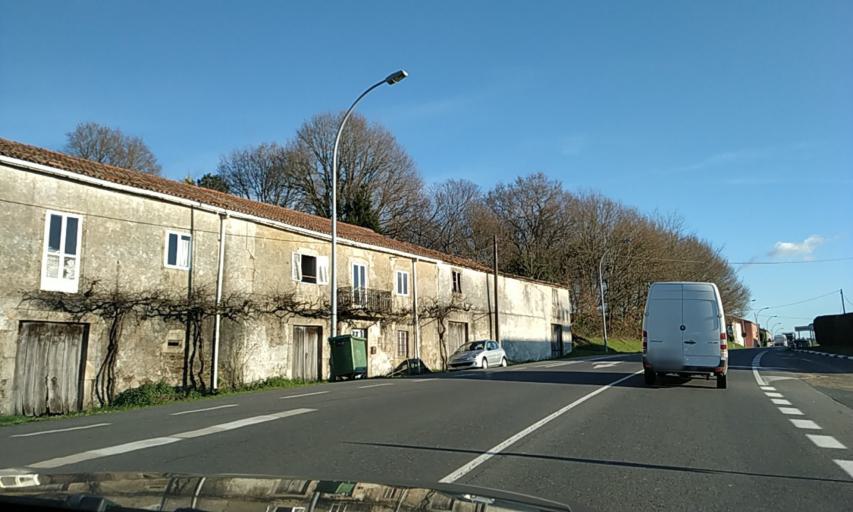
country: ES
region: Galicia
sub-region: Provincia de Pontevedra
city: Lalin
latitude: 42.6815
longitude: -8.1672
